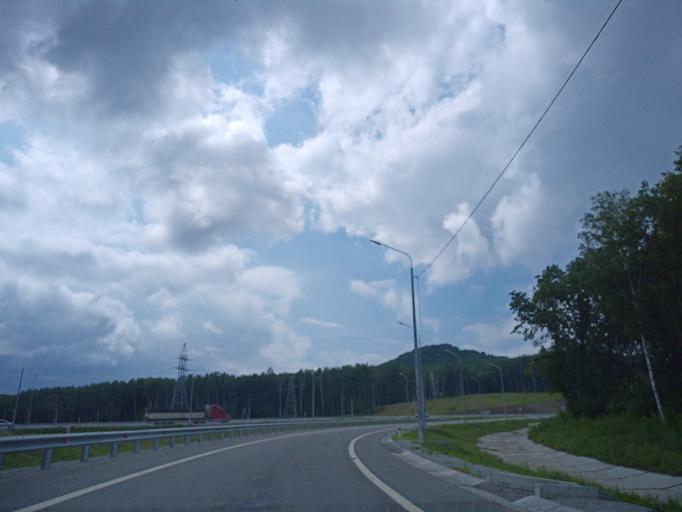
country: RU
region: Khabarovsk Krai
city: Korfovskiy
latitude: 48.2892
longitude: 135.0728
